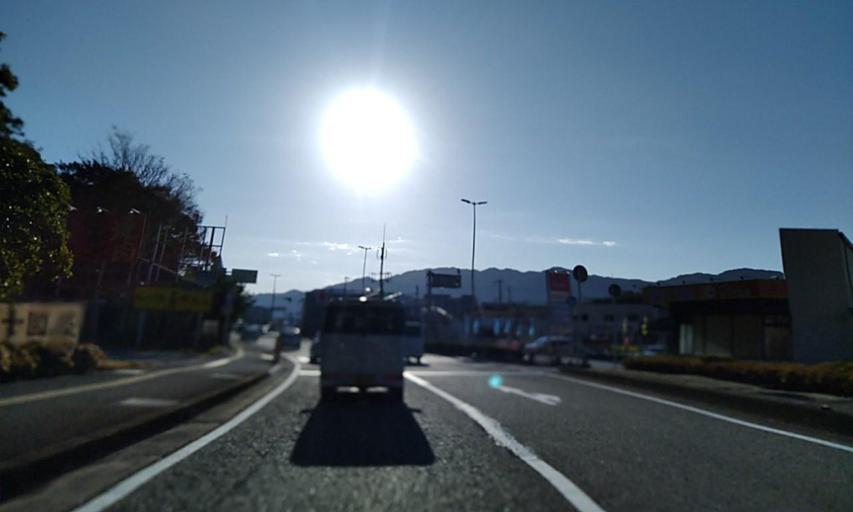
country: JP
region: Wakayama
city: Kainan
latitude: 34.1608
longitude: 135.1909
